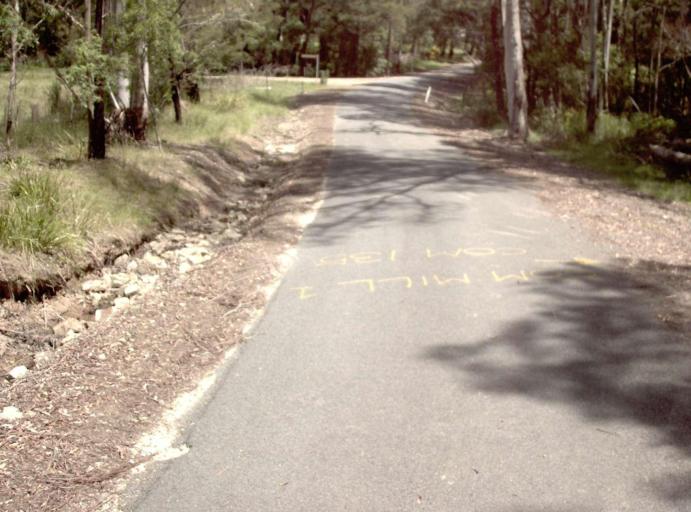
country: AU
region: New South Wales
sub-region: Bombala
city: Bombala
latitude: -37.4257
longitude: 149.0088
